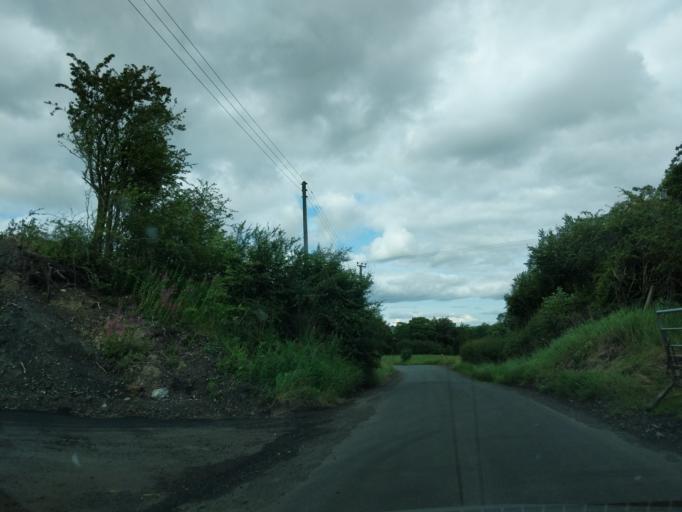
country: GB
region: Scotland
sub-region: South Lanarkshire
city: Dalserf
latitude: 55.7206
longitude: -3.9225
